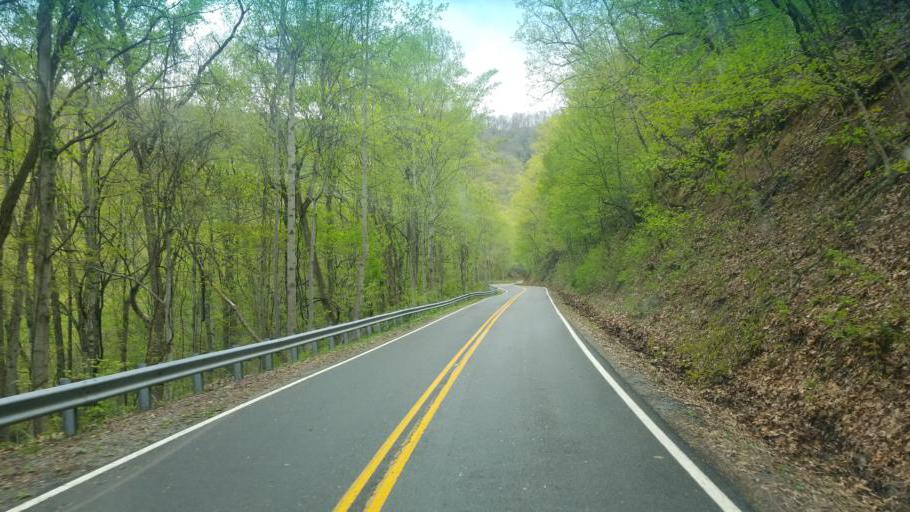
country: US
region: Virginia
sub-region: Tazewell County
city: Tazewell
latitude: 37.0093
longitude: -81.5181
